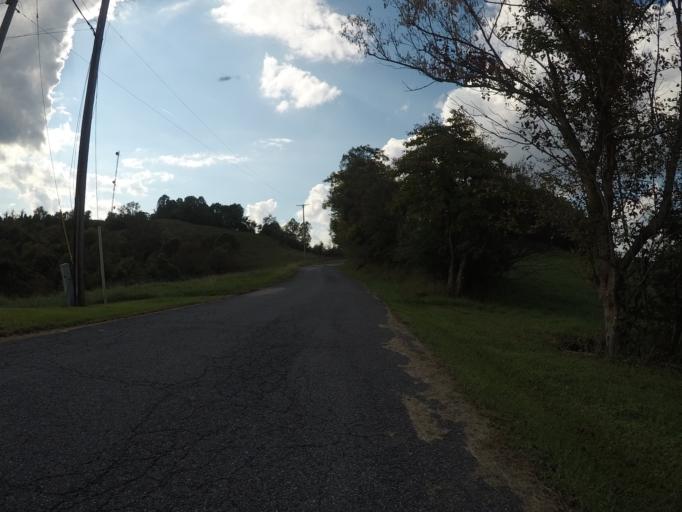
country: US
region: West Virginia
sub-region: Wayne County
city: Lavalette
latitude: 38.3631
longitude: -82.4716
